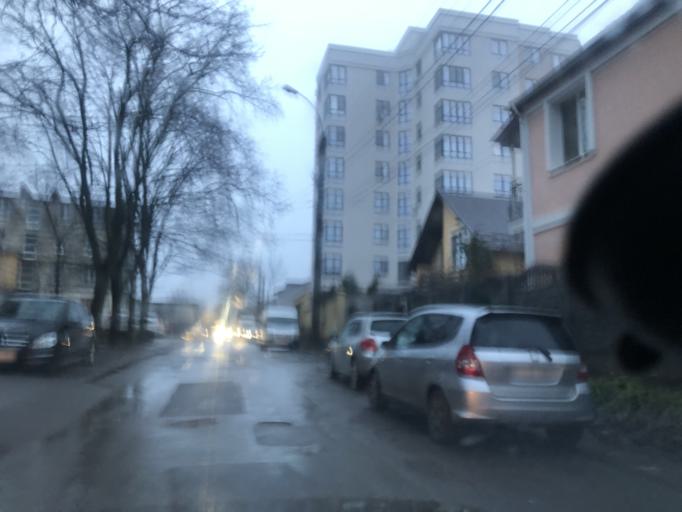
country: MD
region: Chisinau
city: Chisinau
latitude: 46.9819
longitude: 28.8419
